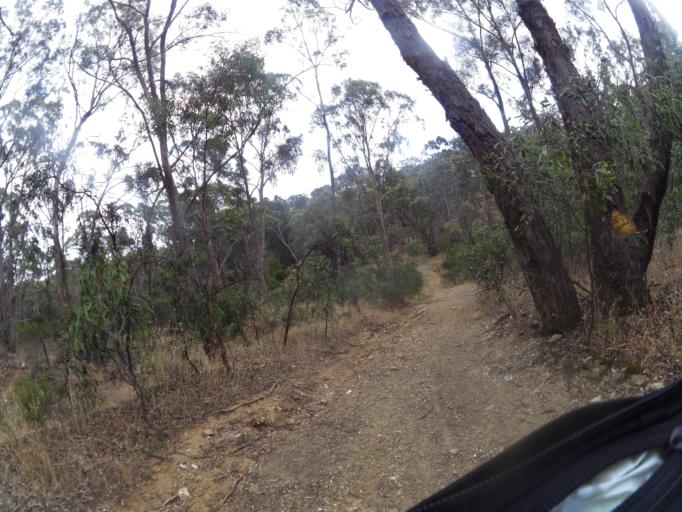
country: AU
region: Victoria
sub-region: Mount Alexander
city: Castlemaine
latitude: -37.0723
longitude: 144.2548
